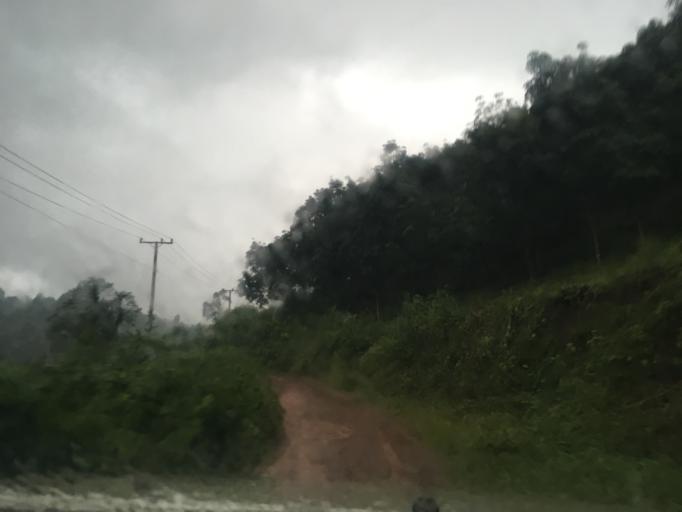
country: LA
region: Oudomxai
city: Muang La
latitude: 21.2417
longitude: 101.9447
